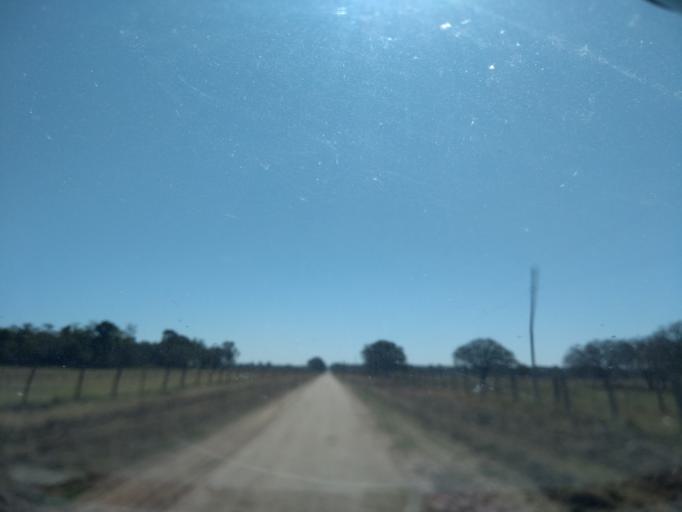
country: AR
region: Chaco
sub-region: Departamento de Quitilipi
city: Quitilipi
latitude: -26.7095
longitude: -60.2227
